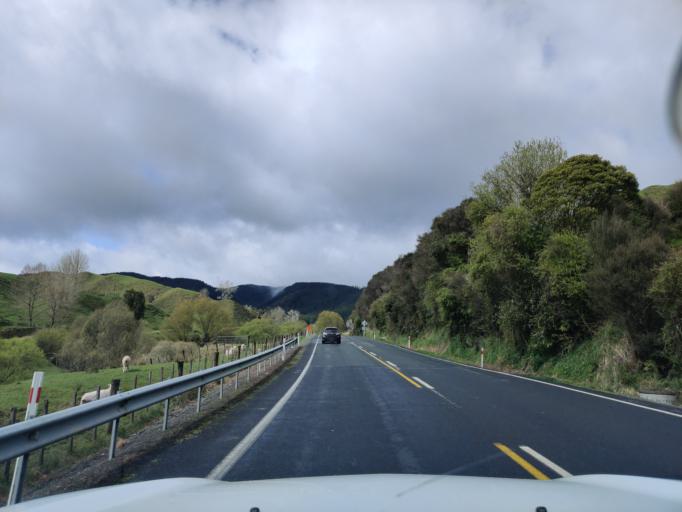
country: NZ
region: Waikato
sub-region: Otorohanga District
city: Otorohanga
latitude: -38.6094
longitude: 175.2169
